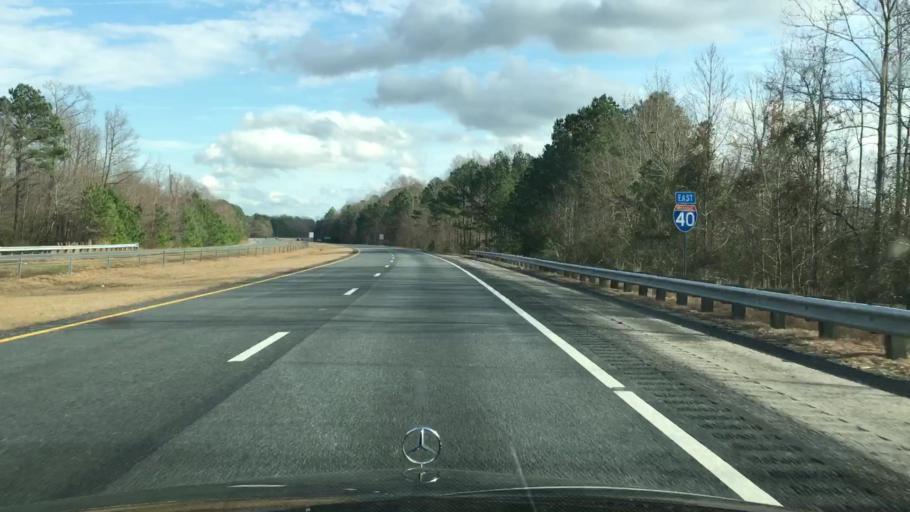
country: US
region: North Carolina
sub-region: Johnston County
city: Four Oaks
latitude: 35.3269
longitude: -78.4400
